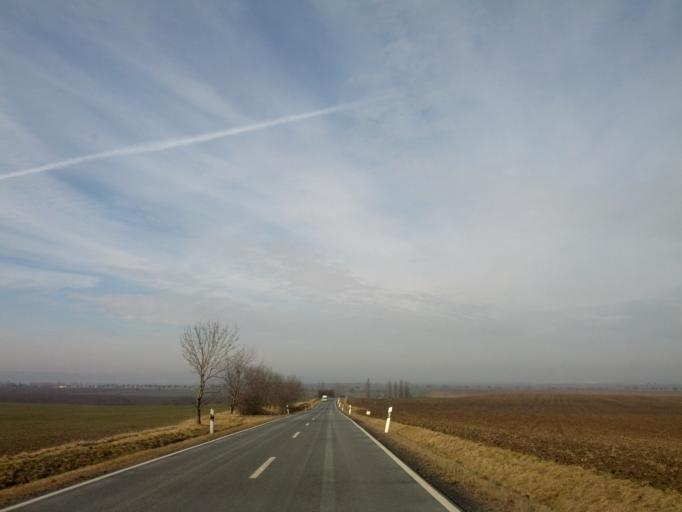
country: DE
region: Thuringia
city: Schonstedt
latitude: 51.1011
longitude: 10.5444
